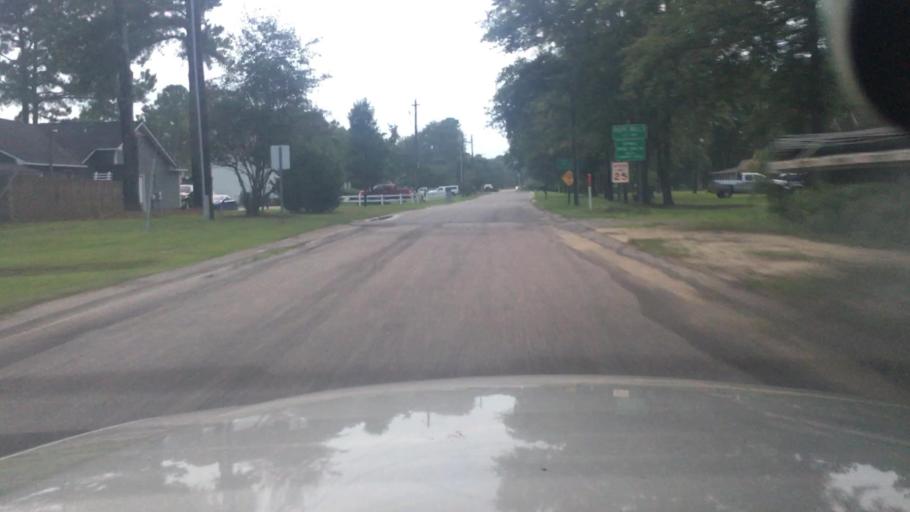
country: US
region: North Carolina
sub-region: Cumberland County
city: Hope Mills
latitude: 34.9623
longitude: -78.9378
